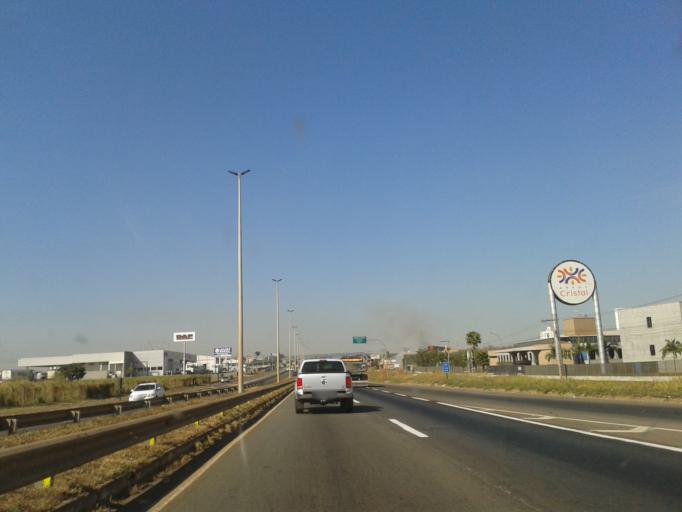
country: BR
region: Goias
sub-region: Aparecida De Goiania
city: Aparecida de Goiania
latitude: -16.8066
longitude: -49.2393
